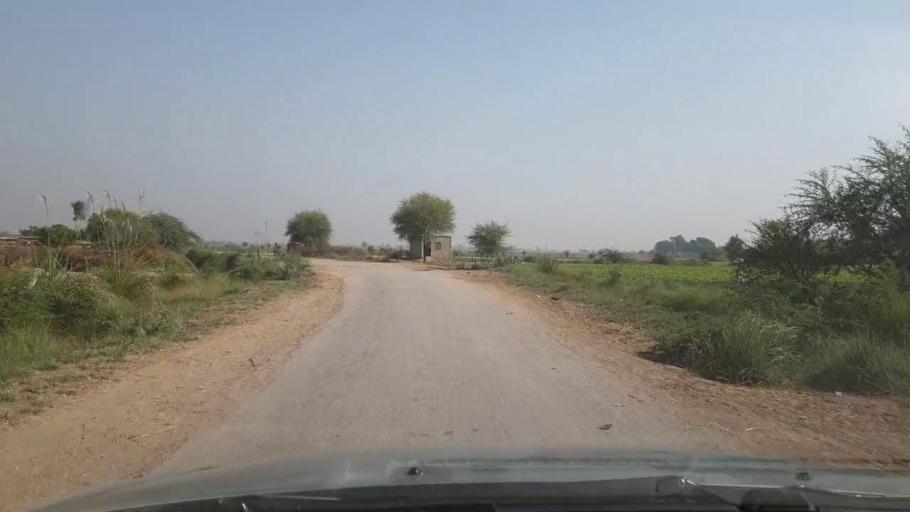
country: PK
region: Sindh
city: Tando Jam
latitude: 25.2856
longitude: 68.5189
